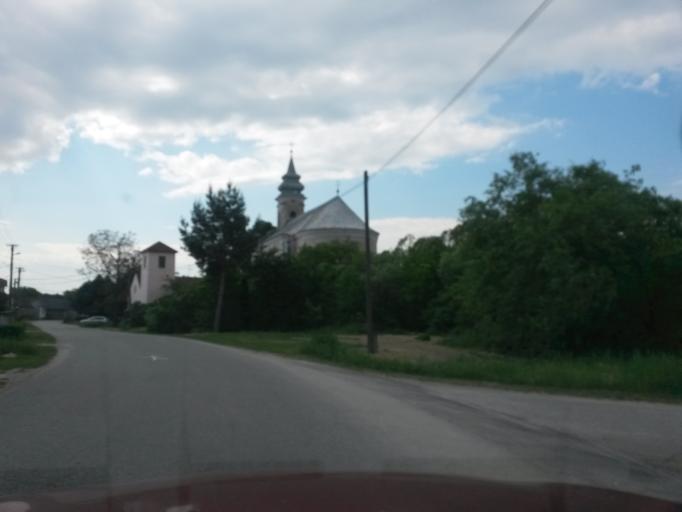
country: SK
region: Kosicky
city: Moldava nad Bodvou
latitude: 48.6917
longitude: 21.0084
